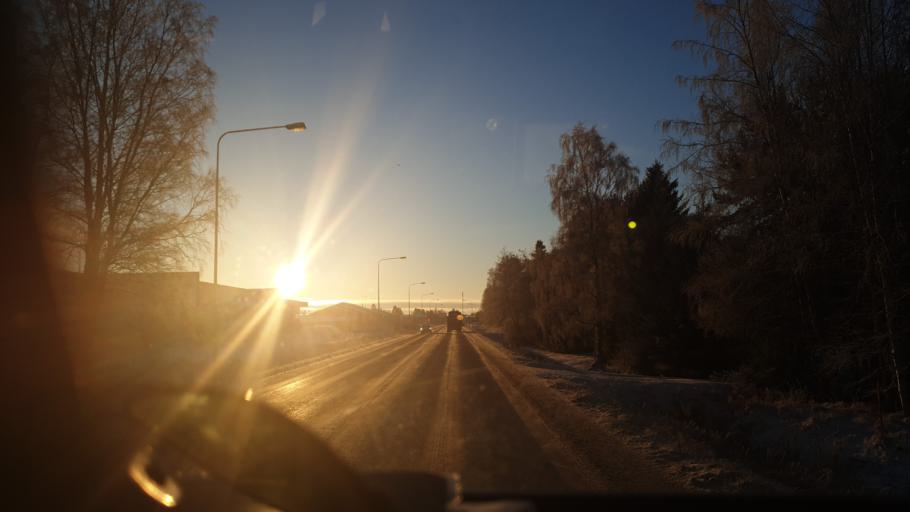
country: FI
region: Northern Ostrobothnia
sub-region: Ylivieska
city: Kalajoki
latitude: 64.2686
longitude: 23.9491
